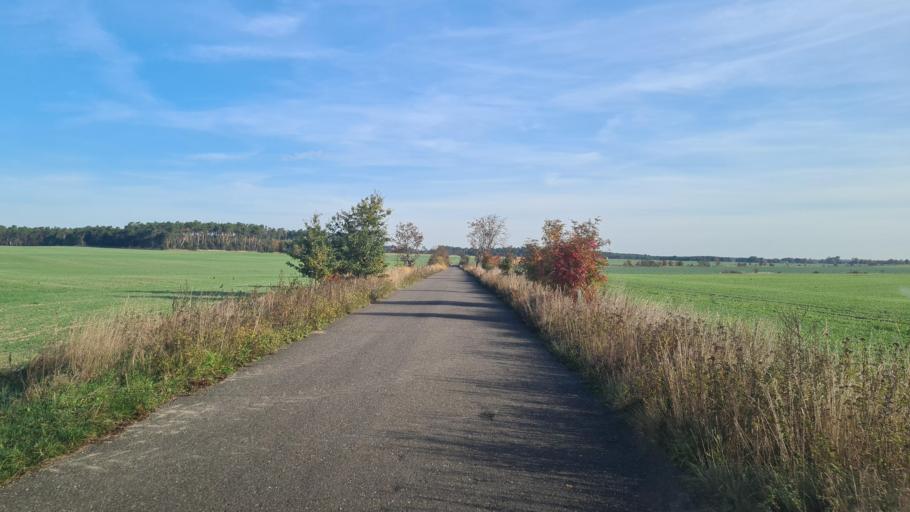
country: DE
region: Brandenburg
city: Ihlow
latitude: 51.8932
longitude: 13.3804
